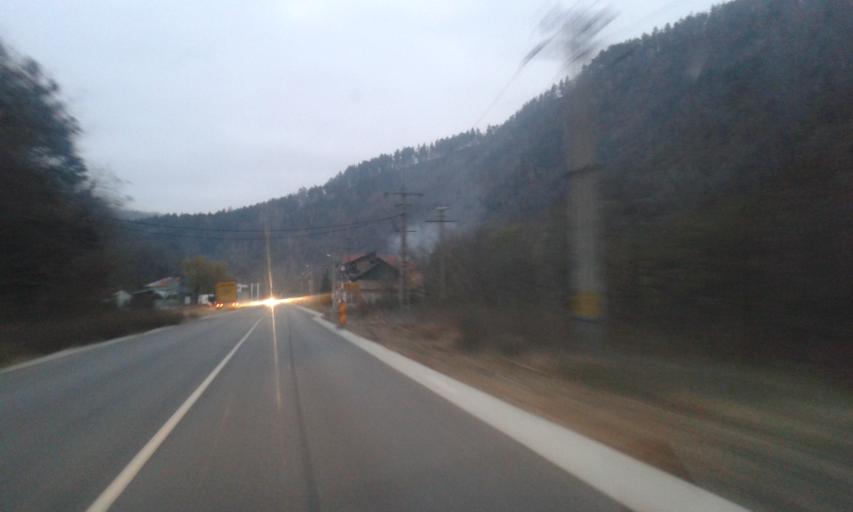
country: RO
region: Gorj
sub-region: Comuna Bumbesti-Jiu
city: Bumbesti-Jiu
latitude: 45.1963
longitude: 23.3824
